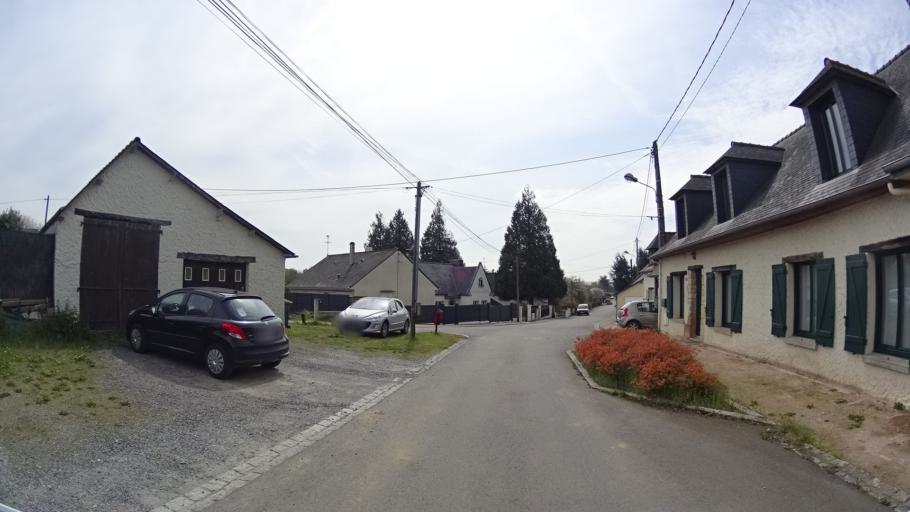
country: FR
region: Brittany
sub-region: Departement d'Ille-et-Vilaine
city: Chartres-de-Bretagne
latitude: 48.0322
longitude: -1.7181
